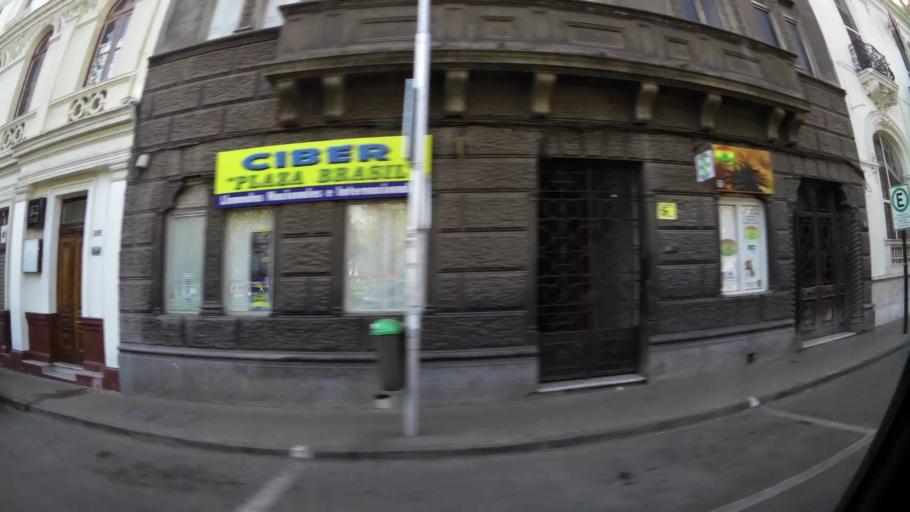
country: CL
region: Santiago Metropolitan
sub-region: Provincia de Santiago
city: Santiago
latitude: -33.4400
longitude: -70.6657
